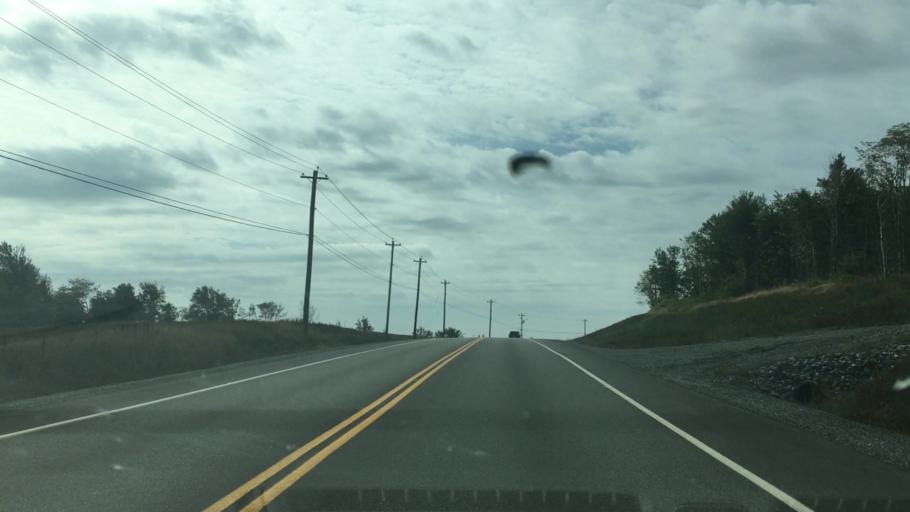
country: CA
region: Nova Scotia
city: Princeville
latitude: 45.6624
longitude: -60.8135
